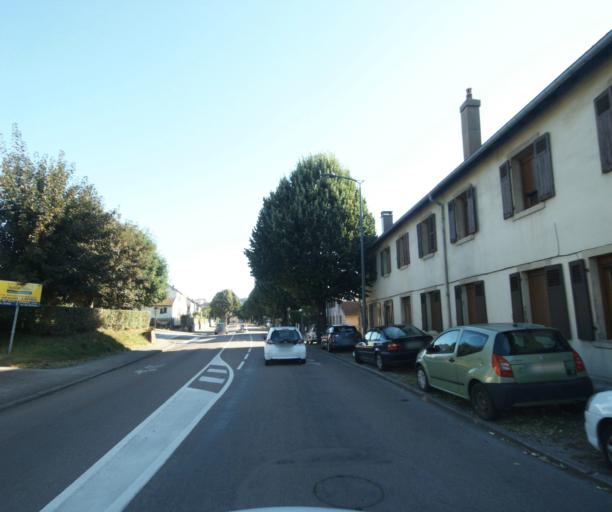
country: FR
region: Lorraine
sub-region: Departement des Vosges
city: Chantraine
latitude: 48.1554
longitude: 6.4510
